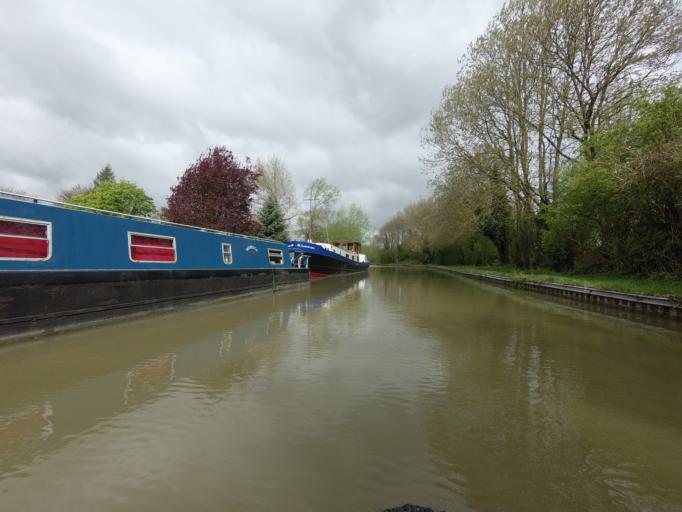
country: GB
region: England
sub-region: Milton Keynes
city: Water Eaton
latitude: 51.9625
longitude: -0.7136
